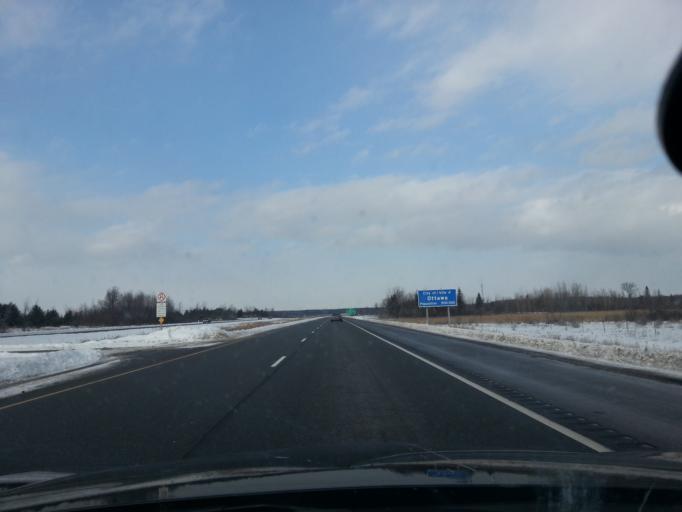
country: CA
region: Ontario
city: Carleton Place
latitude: 45.1861
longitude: -76.0455
